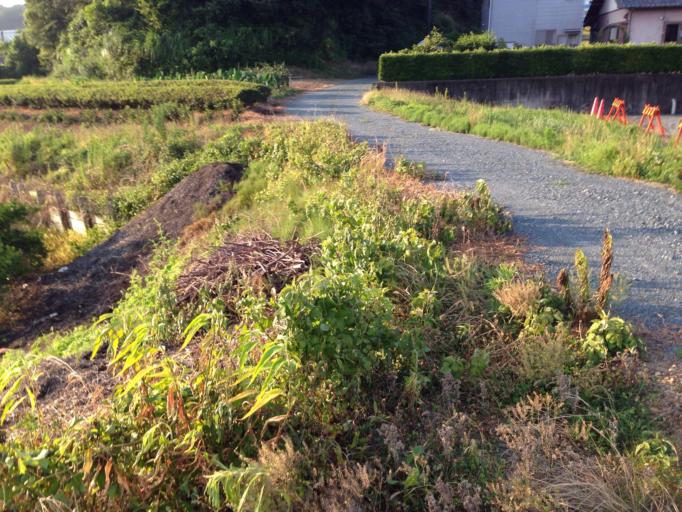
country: JP
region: Shizuoka
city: Fukuroi
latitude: 34.7492
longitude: 137.9484
